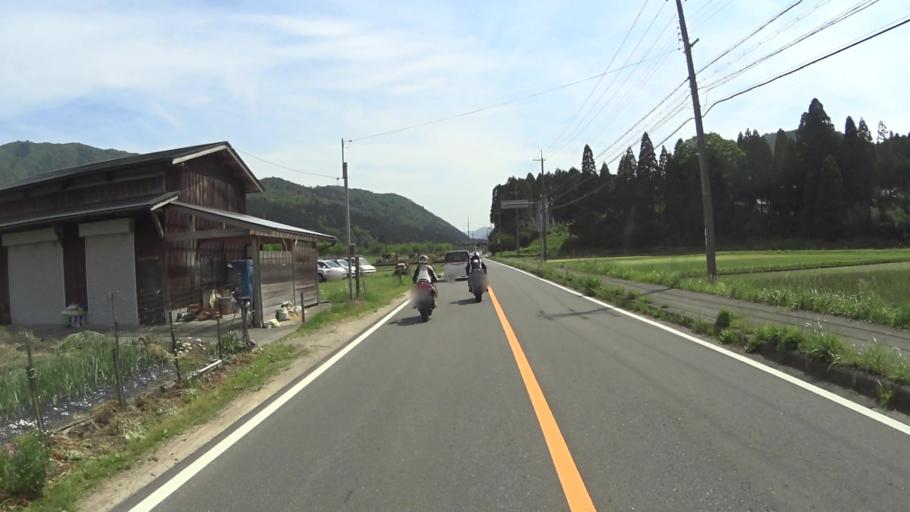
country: JP
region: Shiga Prefecture
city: Kitahama
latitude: 35.3444
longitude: 135.9095
